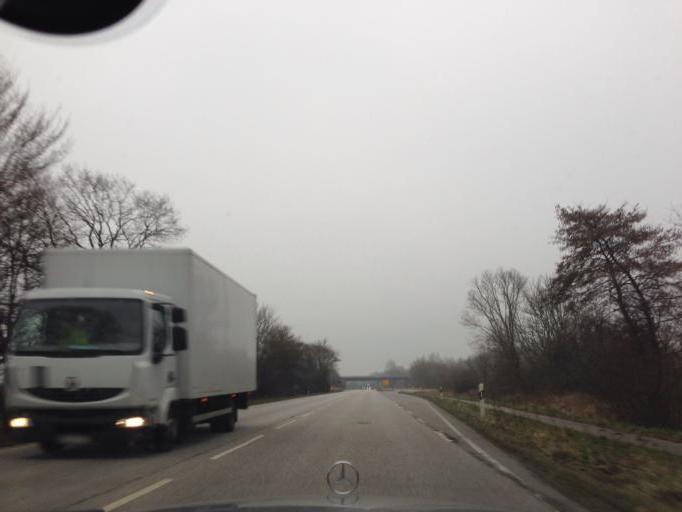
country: DE
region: Schleswig-Holstein
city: Kirchbarkau
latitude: 54.2269
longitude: 10.1463
